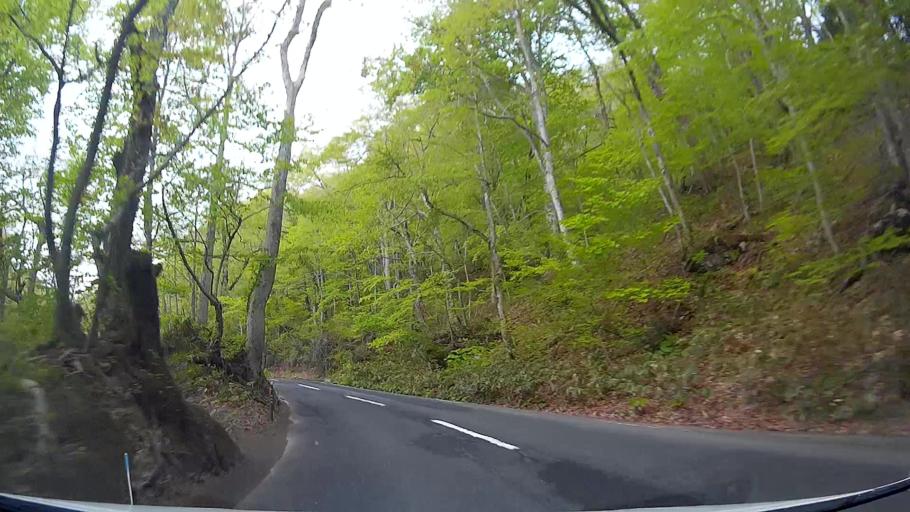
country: JP
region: Aomori
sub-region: Aomori Shi
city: Furudate
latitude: 40.5697
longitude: 140.9791
